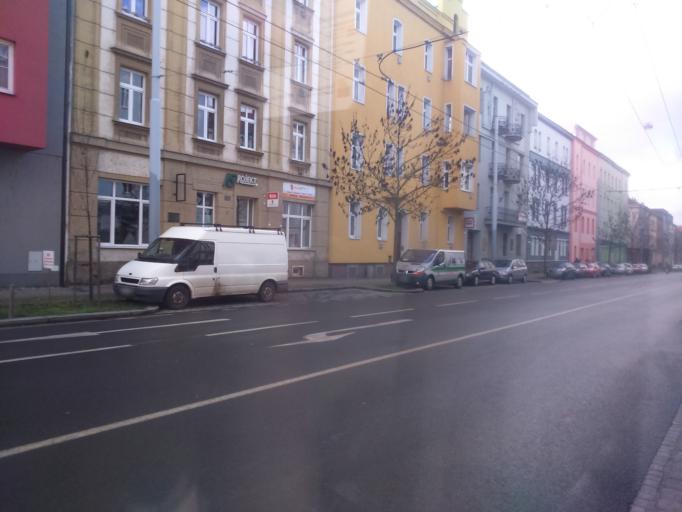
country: CZ
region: Plzensky
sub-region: Okres Plzen-Mesto
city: Pilsen
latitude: 49.7398
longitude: 13.3915
